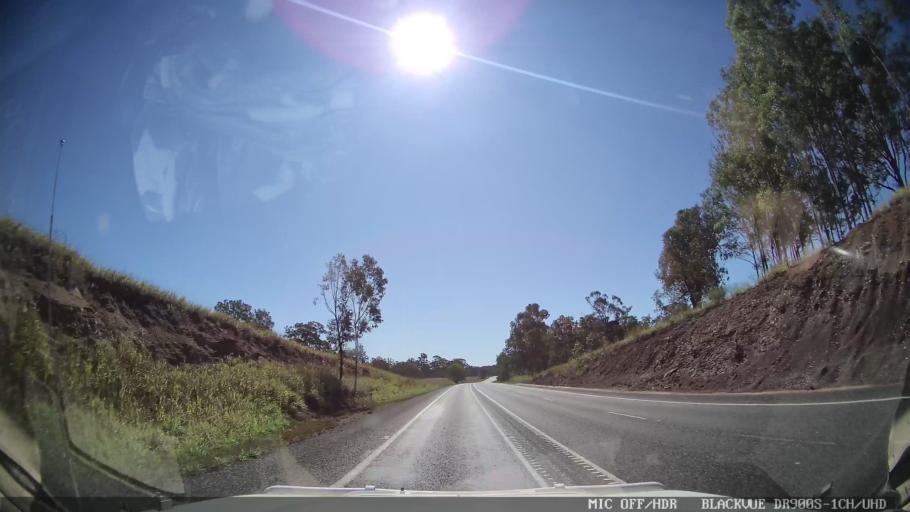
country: AU
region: Queensland
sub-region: Fraser Coast
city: Maryborough
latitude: -25.7719
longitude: 152.5967
